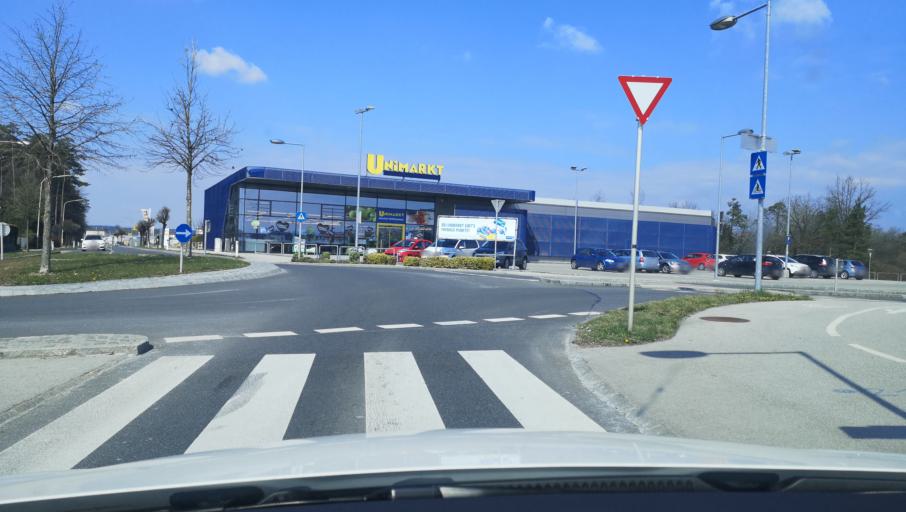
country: AT
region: Lower Austria
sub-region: Politischer Bezirk Amstetten
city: Winklarn
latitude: 48.0803
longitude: 14.8107
